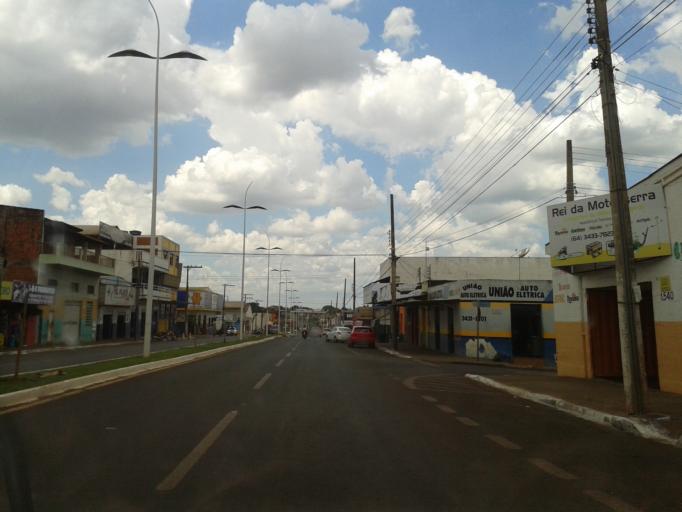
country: BR
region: Goias
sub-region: Itumbiara
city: Itumbiara
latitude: -18.4045
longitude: -49.2090
